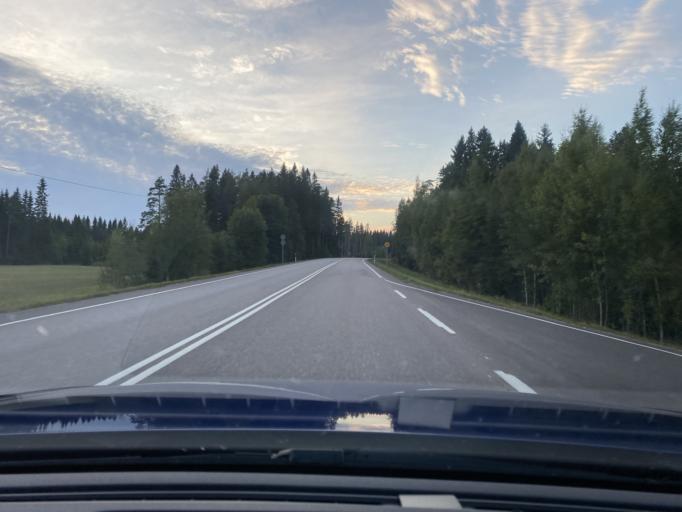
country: FI
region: Satakunta
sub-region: Pohjois-Satakunta
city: Kankaanpaeae
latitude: 61.8581
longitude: 22.3227
